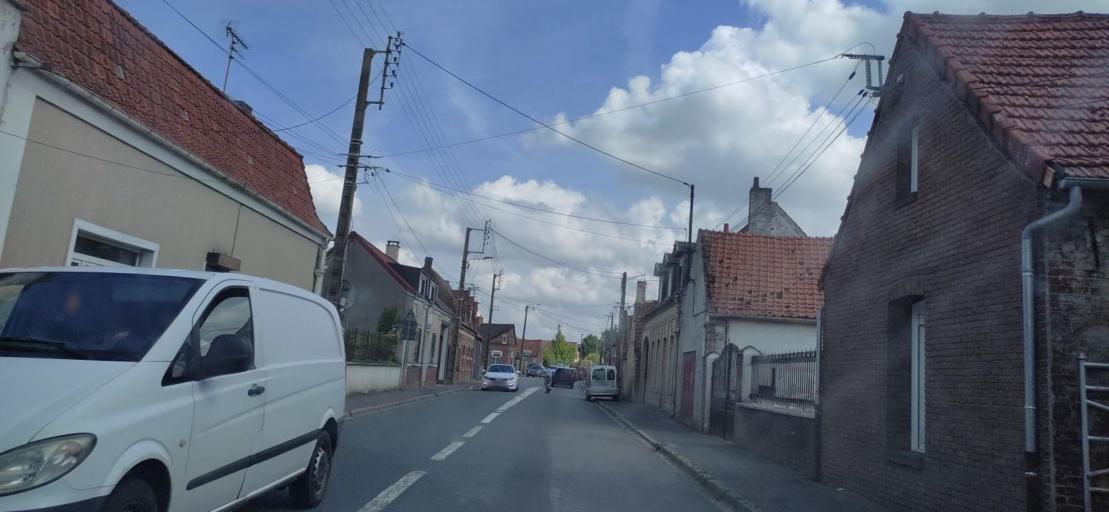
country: FR
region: Nord-Pas-de-Calais
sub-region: Departement du Pas-de-Calais
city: Therouanne
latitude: 50.6344
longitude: 2.2618
